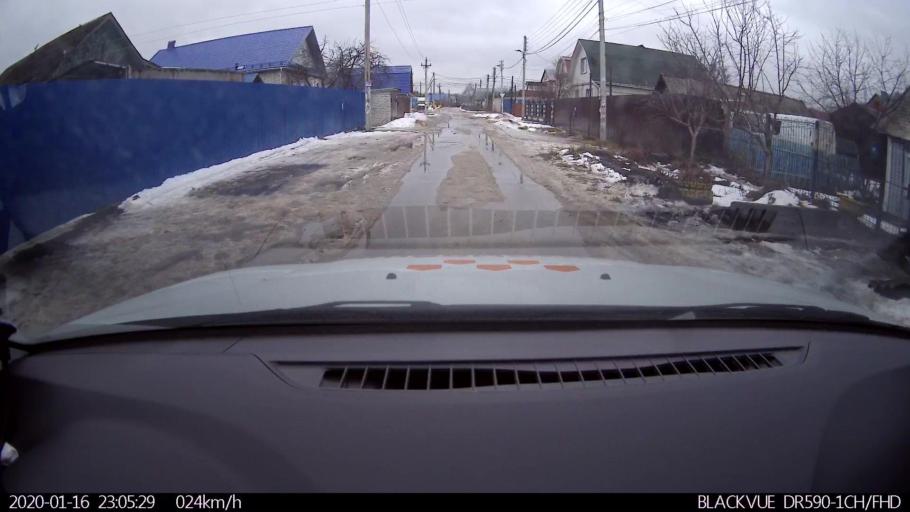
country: RU
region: Nizjnij Novgorod
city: Nizhniy Novgorod
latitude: 56.2847
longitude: 43.9018
